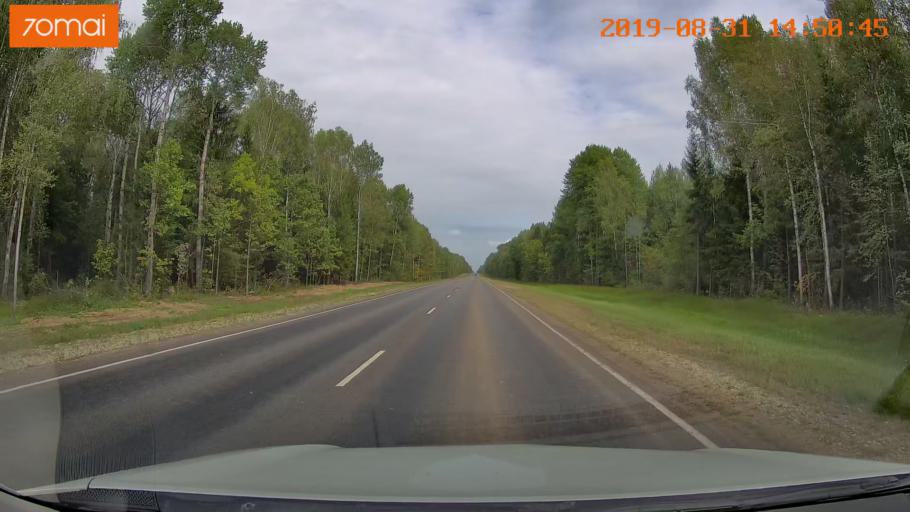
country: RU
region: Kaluga
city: Spas-Demensk
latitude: 54.2637
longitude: 33.7977
